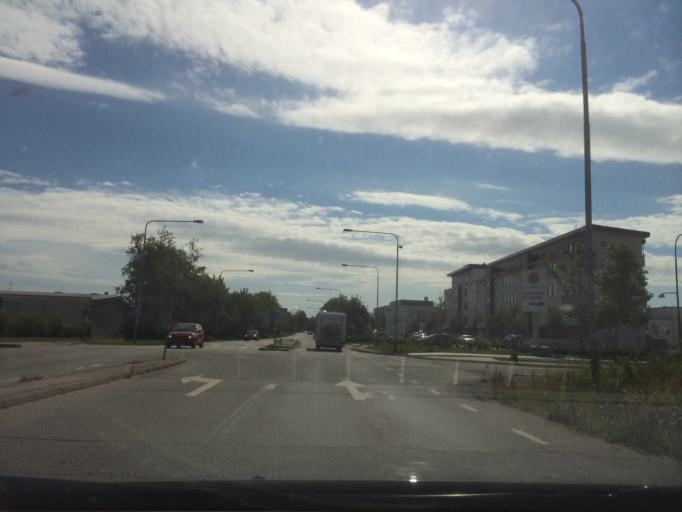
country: SE
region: Skane
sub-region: Malmo
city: Bunkeflostrand
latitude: 55.5736
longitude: 12.9294
